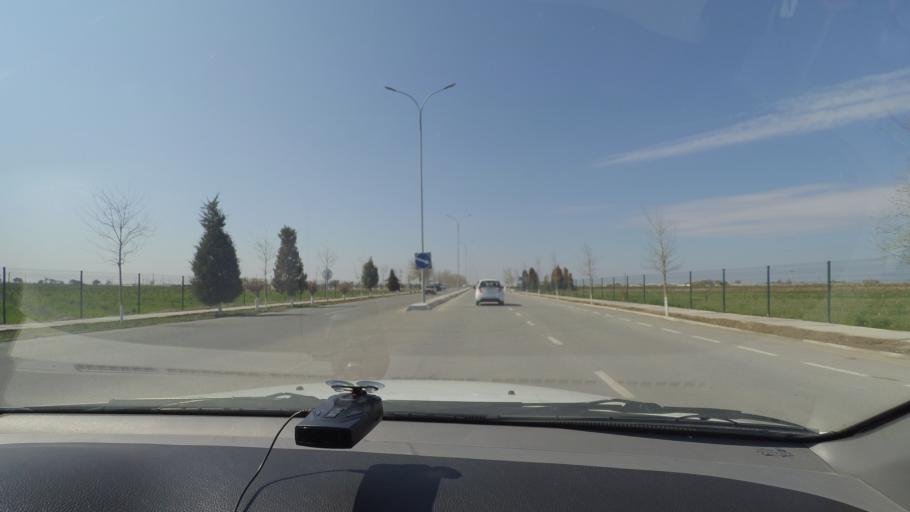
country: UZ
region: Bukhara
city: Bukhara
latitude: 39.8021
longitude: 64.4910
